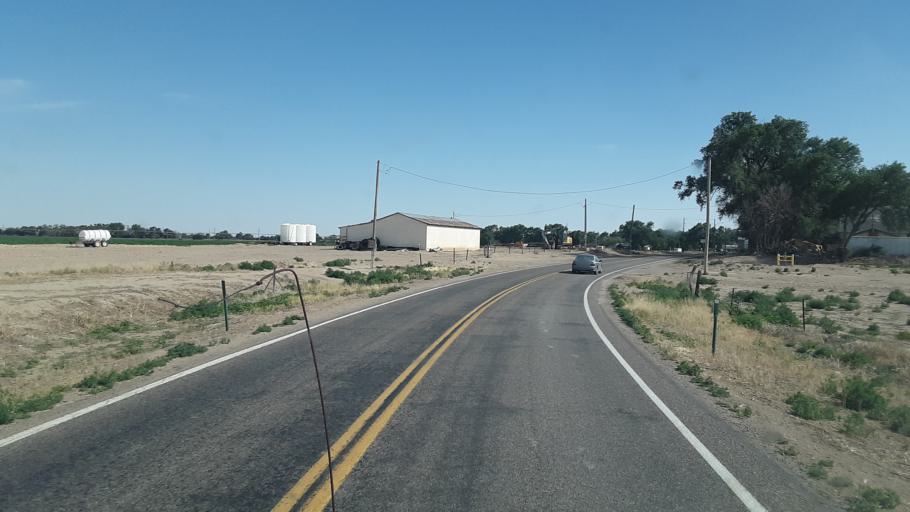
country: US
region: Colorado
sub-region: Crowley County
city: Ordway
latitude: 38.1141
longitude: -103.8640
